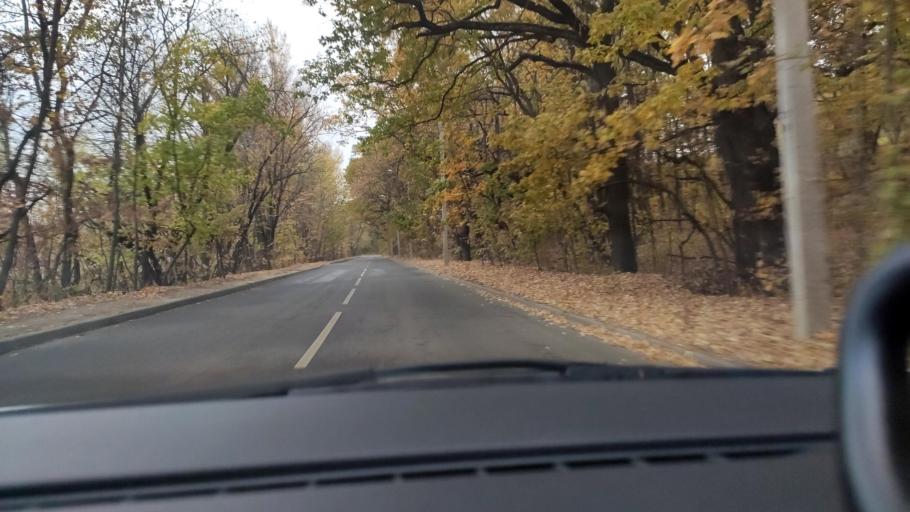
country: RU
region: Voronezj
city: Voronezh
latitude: 51.7245
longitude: 39.2351
